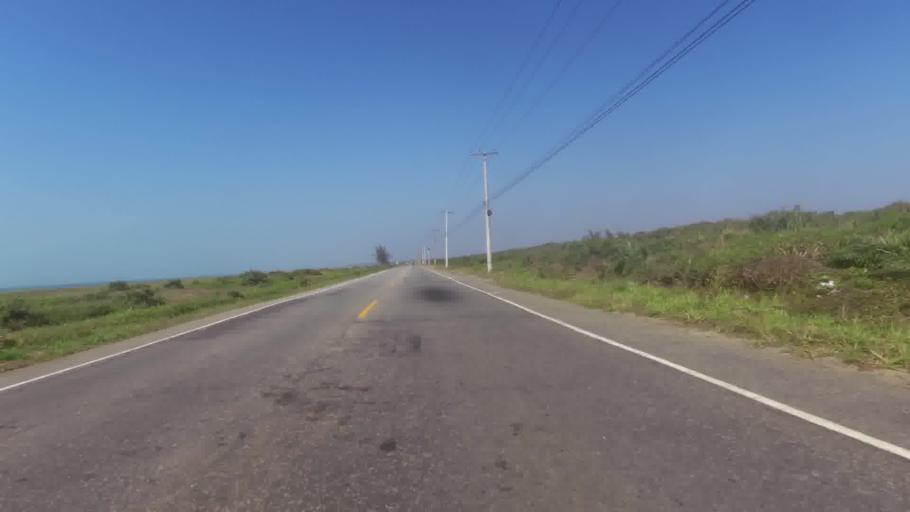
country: BR
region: Espirito Santo
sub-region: Itapemirim
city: Itapemirim
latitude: -20.9459
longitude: -40.8057
